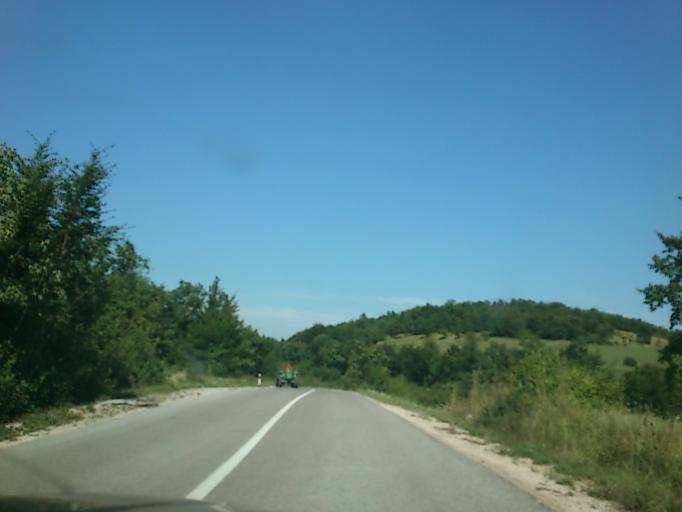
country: HR
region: Licko-Senjska
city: Otocac
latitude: 44.8450
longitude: 15.1145
